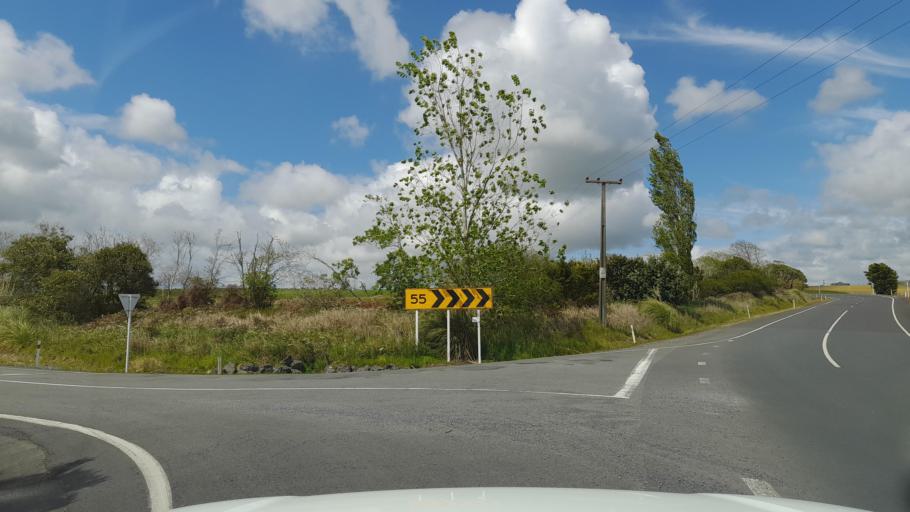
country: NZ
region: Northland
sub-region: Whangarei
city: Maungatapere
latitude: -35.7324
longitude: 174.0691
